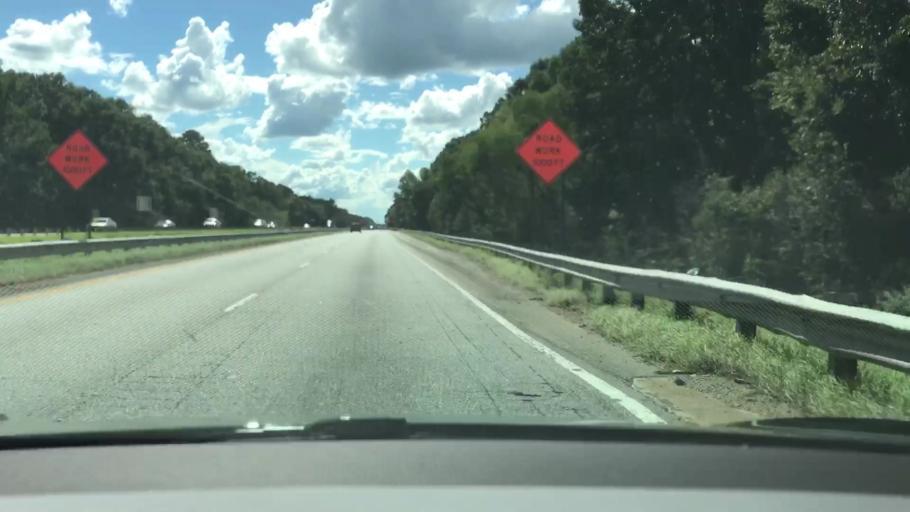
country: US
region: Alabama
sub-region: Montgomery County
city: Pike Road
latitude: 32.3820
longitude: -86.0073
